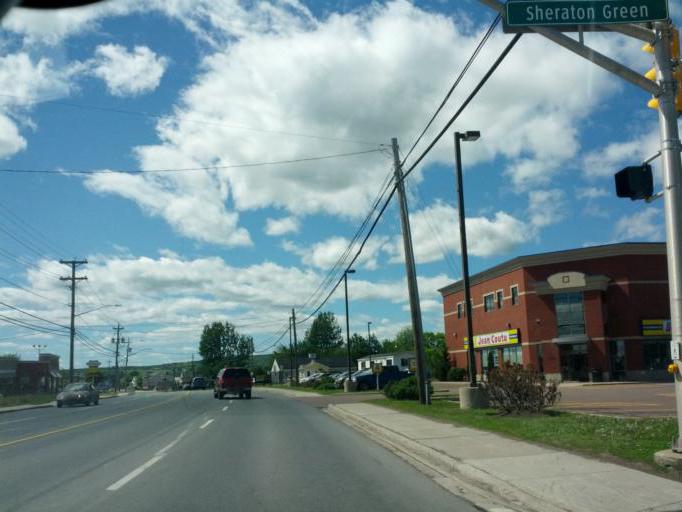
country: CA
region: New Brunswick
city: Moncton
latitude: 46.1210
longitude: -64.8457
